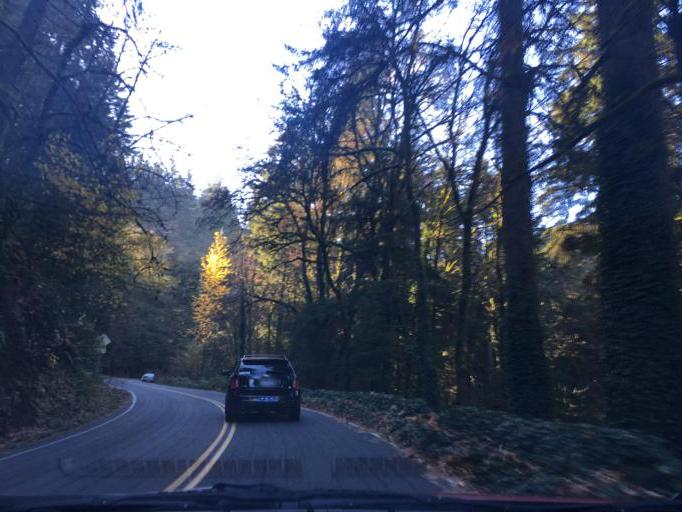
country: US
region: Oregon
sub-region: Washington County
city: Cedar Mill
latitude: 45.5898
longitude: -122.7844
